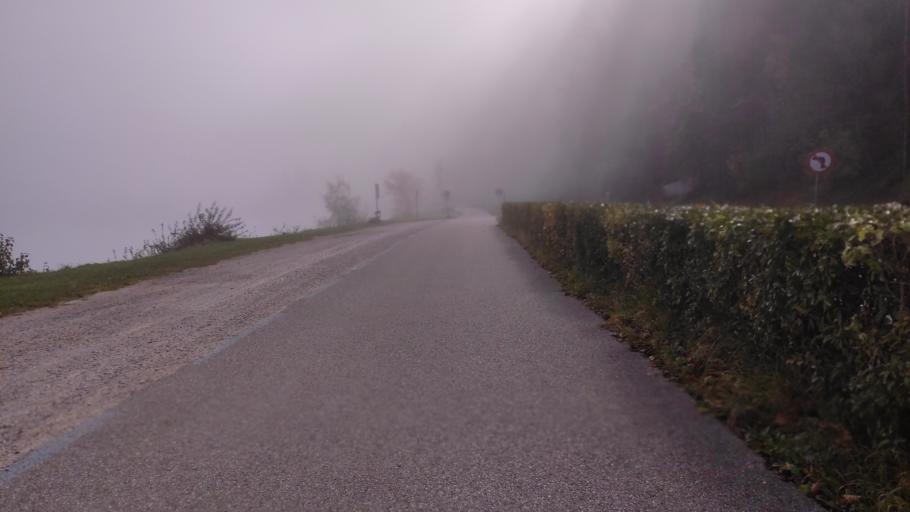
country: AT
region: Salzburg
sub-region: Politischer Bezirk Salzburg-Umgebung
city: Sankt Gilgen
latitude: 47.7407
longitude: 13.3915
